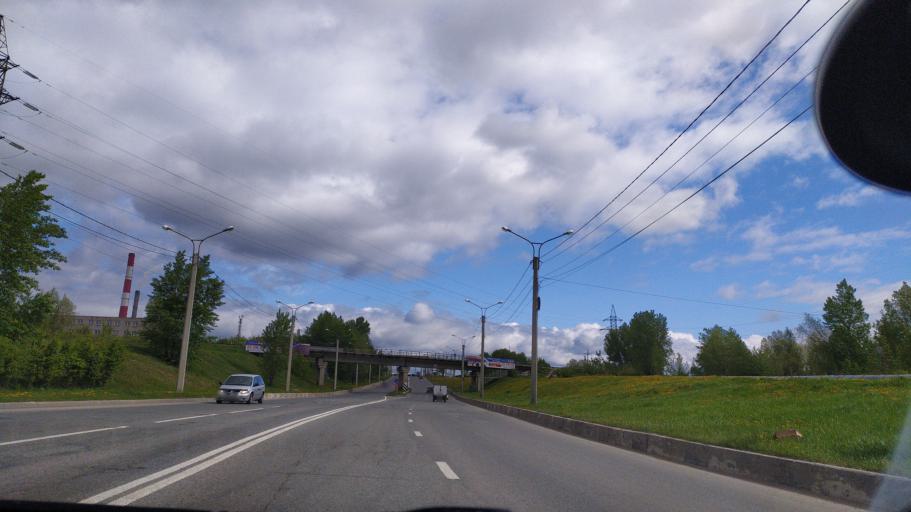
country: RU
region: Chuvashia
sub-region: Cheboksarskiy Rayon
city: Cheboksary
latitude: 56.1119
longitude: 47.2961
